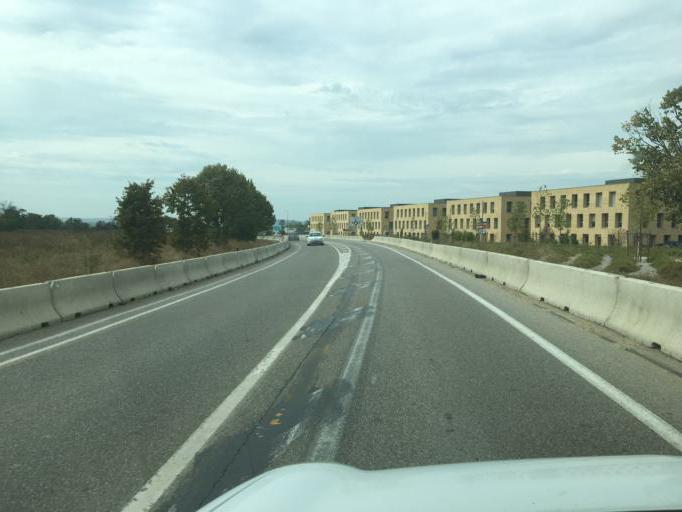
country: FR
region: Provence-Alpes-Cote d'Azur
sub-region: Departement des Bouches-du-Rhone
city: Bouc-Bel-Air
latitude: 43.4780
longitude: 5.3966
